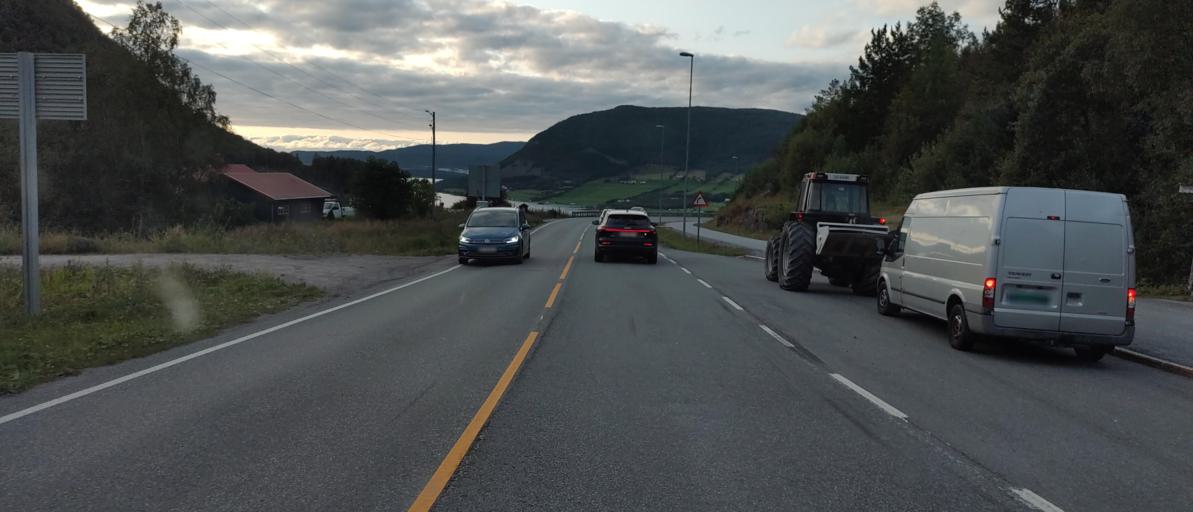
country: NO
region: More og Romsdal
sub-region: Molde
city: Molde
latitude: 62.7939
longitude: 7.2312
